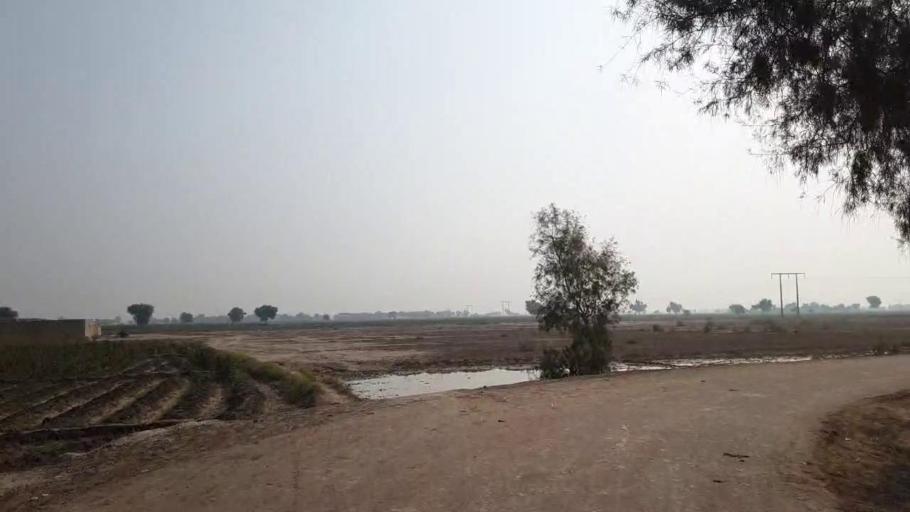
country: PK
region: Sindh
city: Bhan
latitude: 26.4722
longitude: 67.7391
